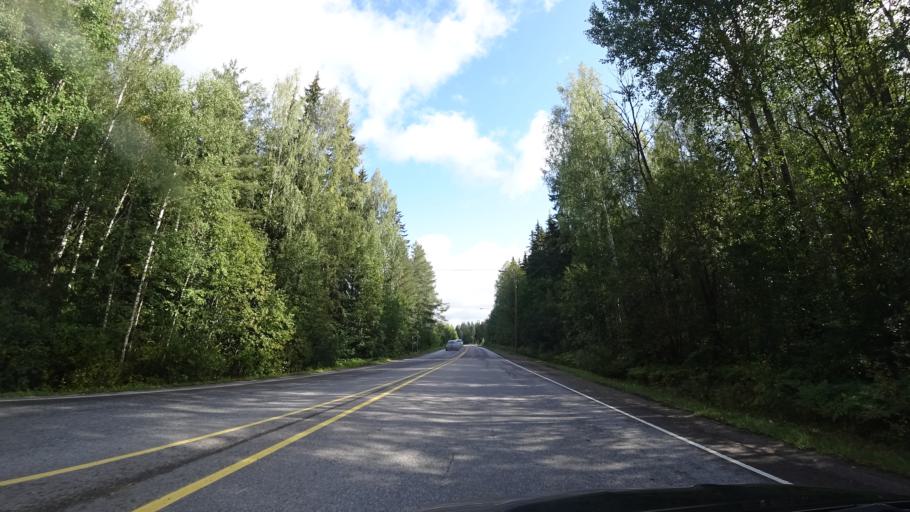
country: FI
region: Uusimaa
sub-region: Helsinki
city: Hyvinge
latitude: 60.5335
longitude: 24.9188
